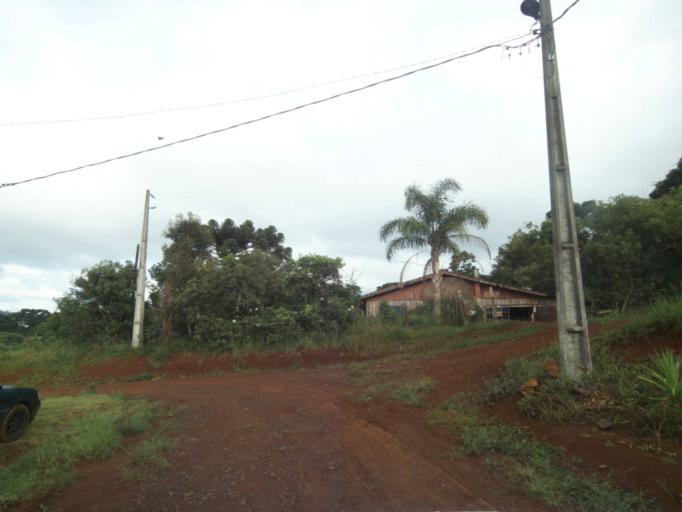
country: BR
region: Parana
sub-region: Pitanga
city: Pitanga
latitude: -24.9382
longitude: -51.8654
